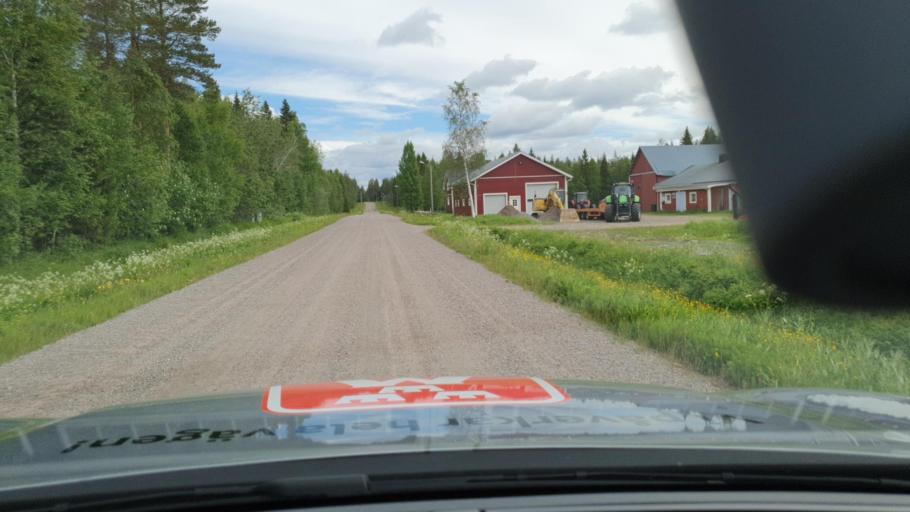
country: FI
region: Lapland
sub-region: Torniolaakso
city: Ylitornio
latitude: 66.0157
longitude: 23.8440
